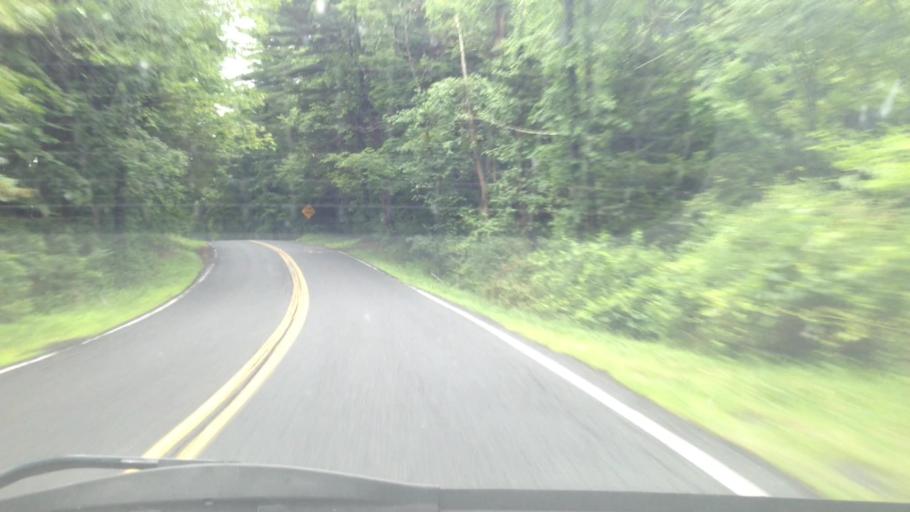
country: US
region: New York
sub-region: Ulster County
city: New Paltz
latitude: 41.7817
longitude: -74.0695
